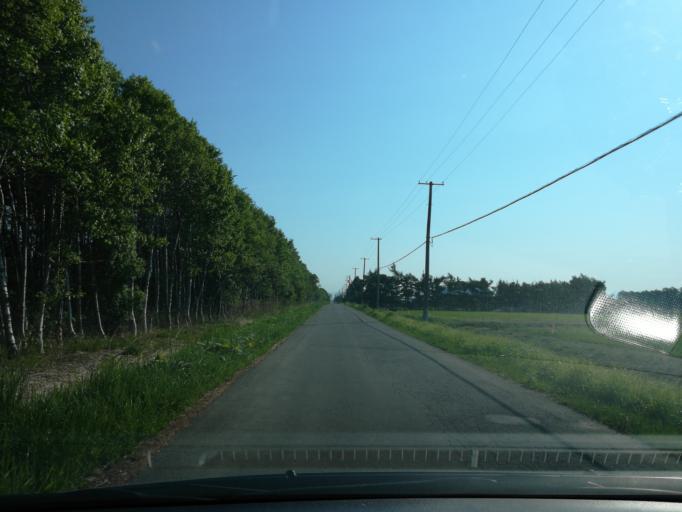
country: JP
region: Hokkaido
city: Ebetsu
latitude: 43.1166
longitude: 141.6483
